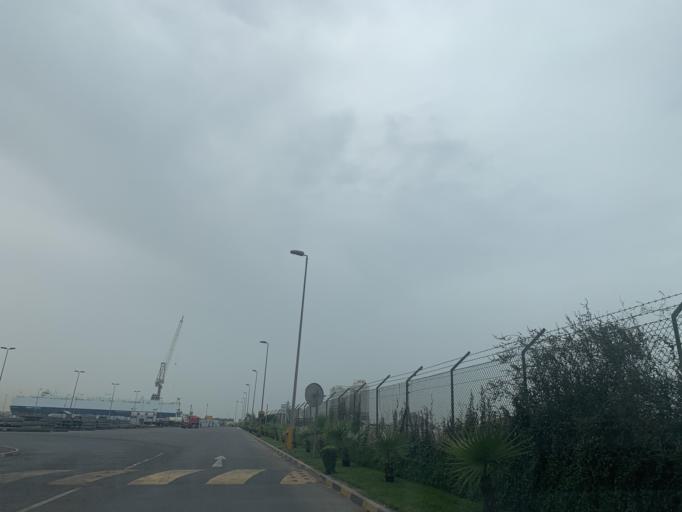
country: BH
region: Muharraq
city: Al Hadd
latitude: 26.2044
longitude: 50.6753
